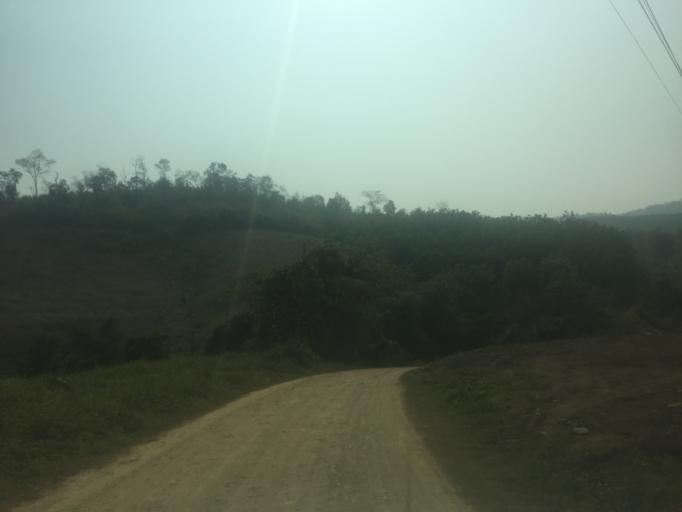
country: TH
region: Phayao
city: Phu Sang
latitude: 19.6307
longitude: 100.5357
